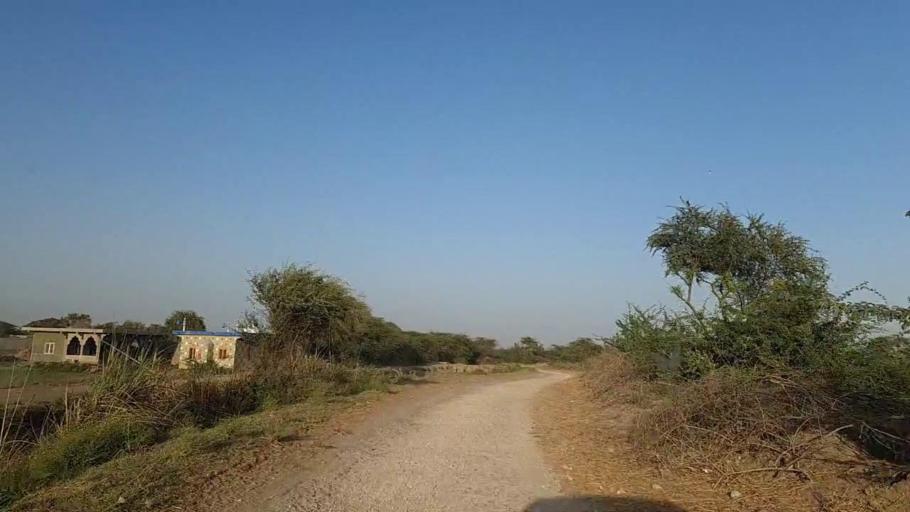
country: PK
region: Sindh
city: Jati
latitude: 24.4153
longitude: 68.3406
